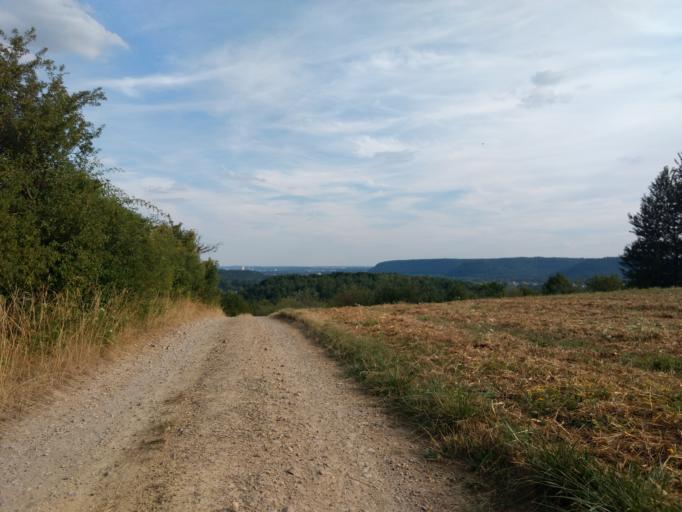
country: DE
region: Saarland
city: Beckingen
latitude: 49.3990
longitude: 6.6953
